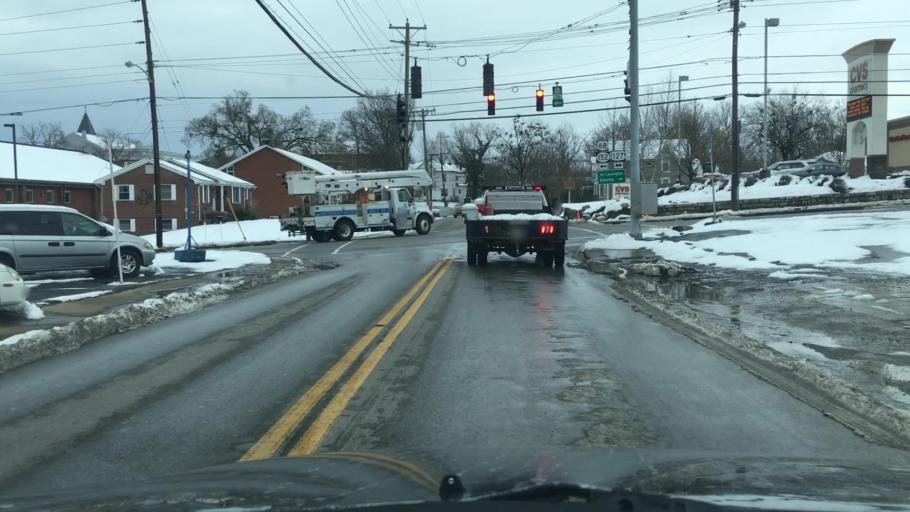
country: US
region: Kentucky
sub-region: Mercer County
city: Harrodsburg
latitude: 37.7585
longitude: -84.8464
